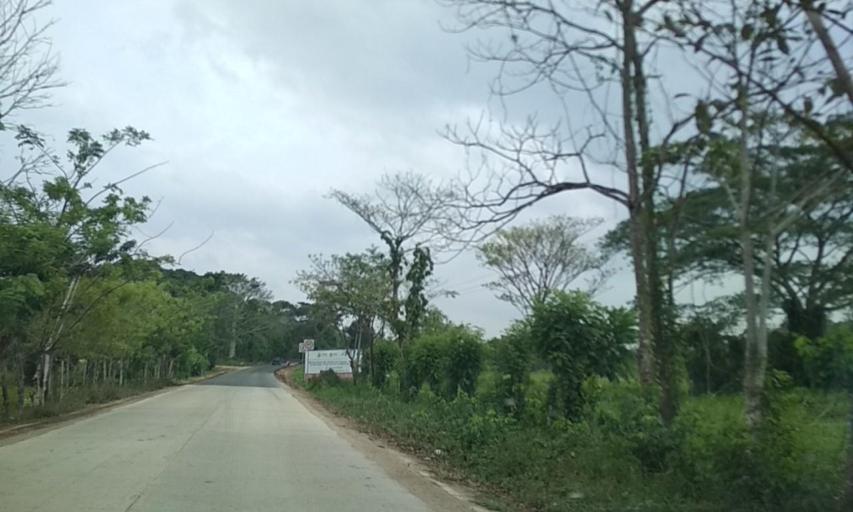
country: MX
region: Tabasco
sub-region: Huimanguillo
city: Francisco Rueda
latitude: 17.6788
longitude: -94.0921
